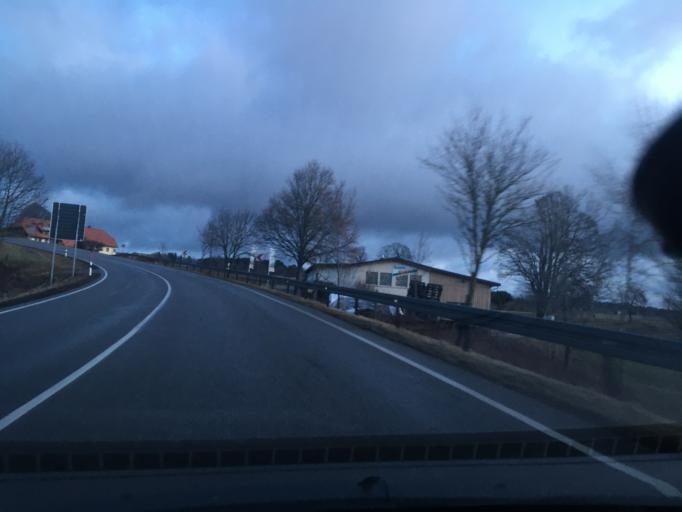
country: DE
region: Baden-Wuerttemberg
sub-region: Freiburg Region
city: Hochenschwand
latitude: 47.7142
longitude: 8.1513
